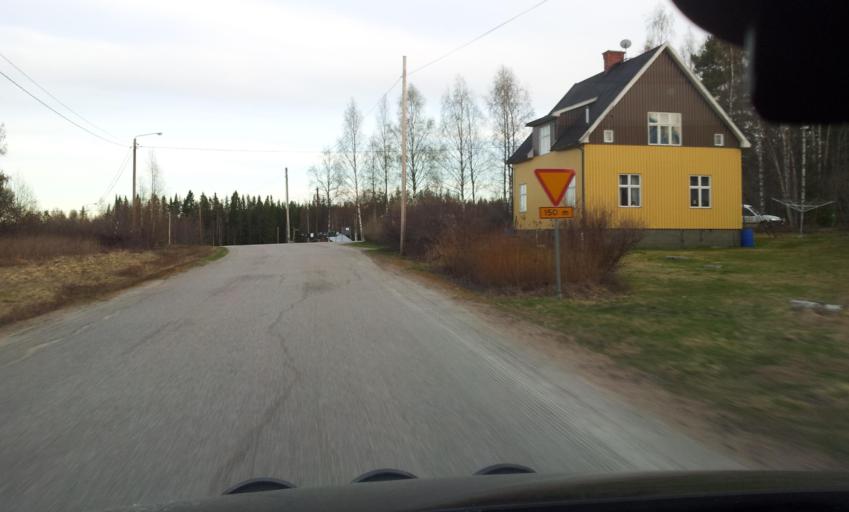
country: SE
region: Gaevleborg
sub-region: Ljusdals Kommun
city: Farila
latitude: 62.0023
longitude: 15.8380
